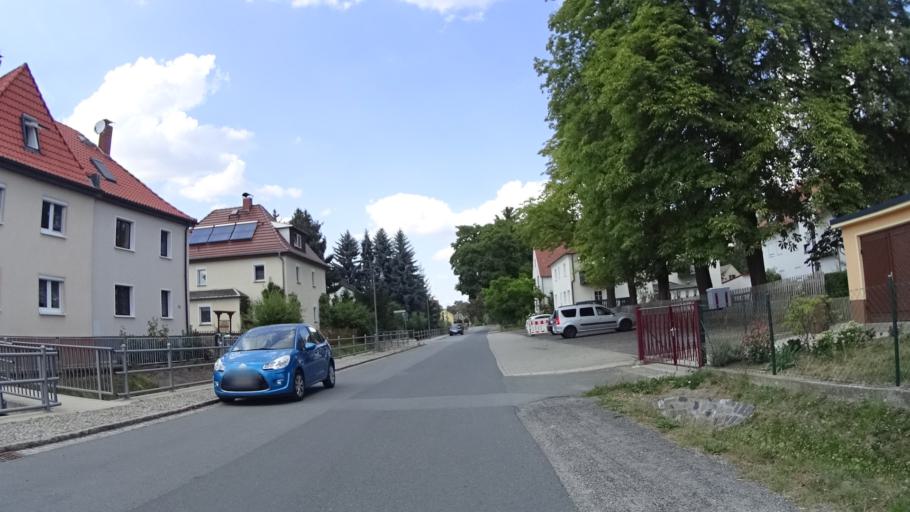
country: DE
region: Saxony
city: Ostritz
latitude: 51.0089
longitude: 14.9324
